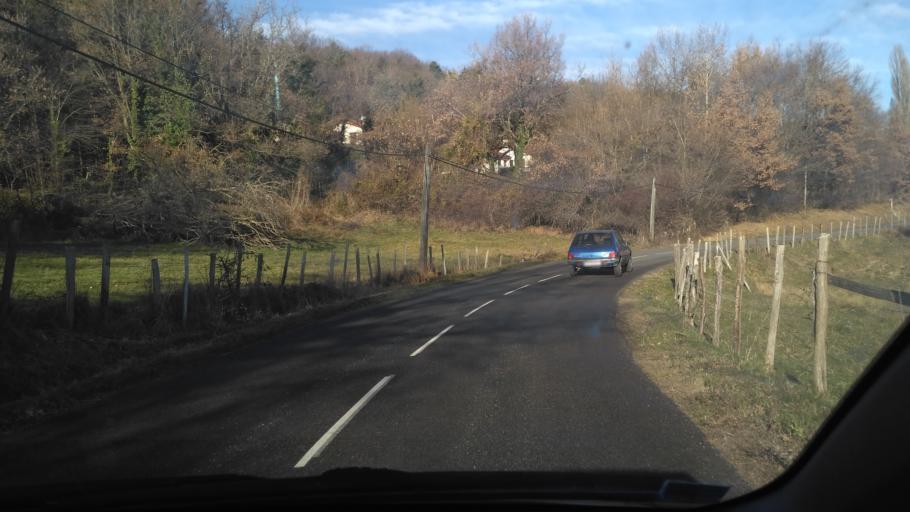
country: FR
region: Rhone-Alpes
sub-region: Departement de l'Isere
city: Saint-Antoine-l'Abbaye
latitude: 45.1669
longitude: 5.2004
